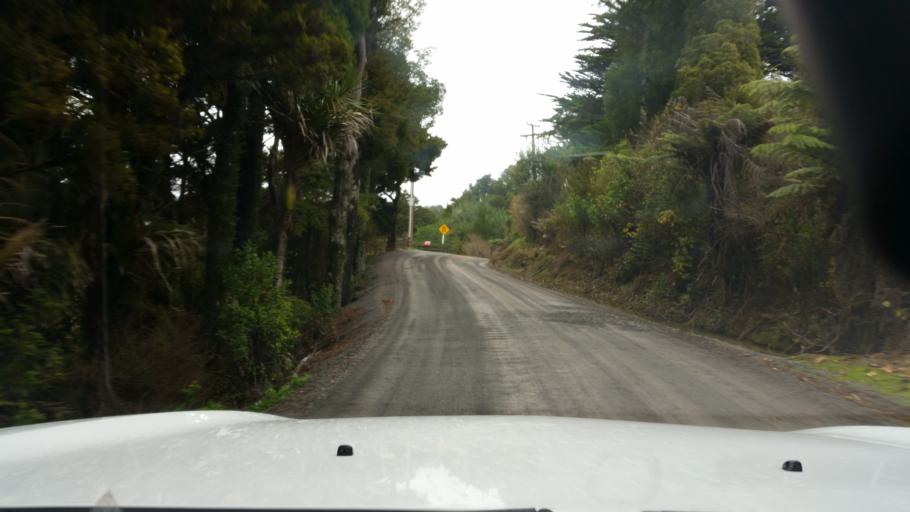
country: NZ
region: Northland
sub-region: Whangarei
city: Whangarei
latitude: -35.7314
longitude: 174.4255
